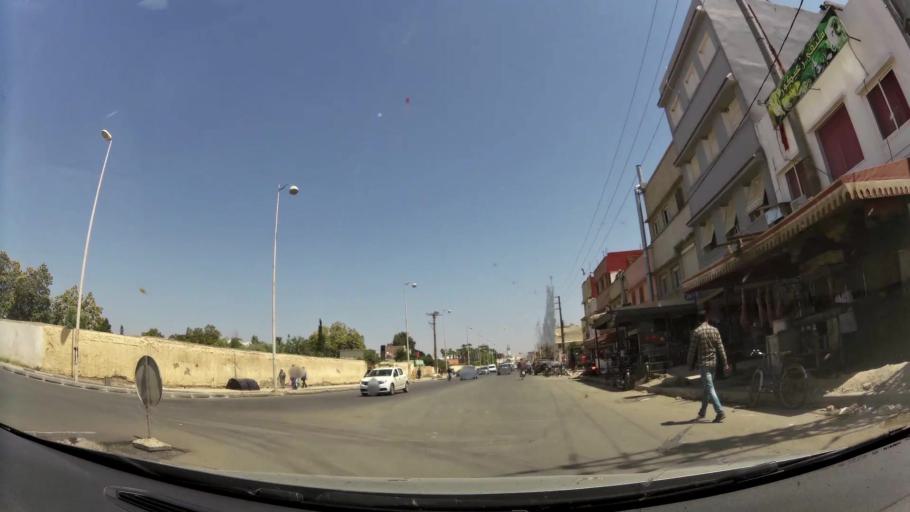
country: MA
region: Rabat-Sale-Zemmour-Zaer
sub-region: Khemisset
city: Khemisset
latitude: 33.8212
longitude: -6.0723
